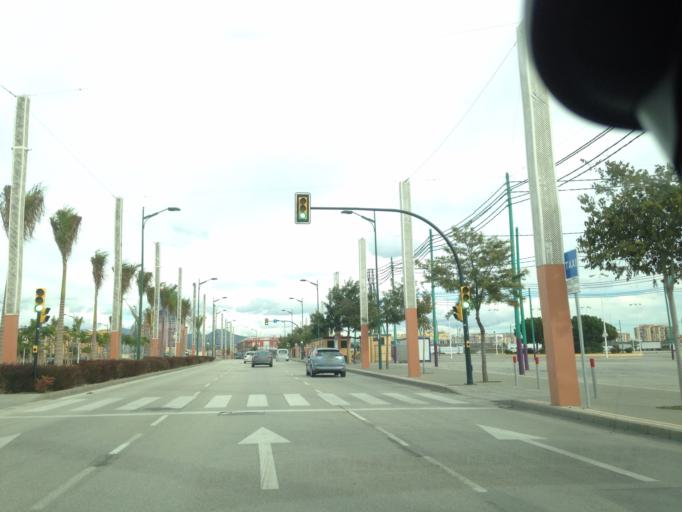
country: ES
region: Andalusia
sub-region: Provincia de Malaga
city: Malaga
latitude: 36.7011
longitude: -4.4618
